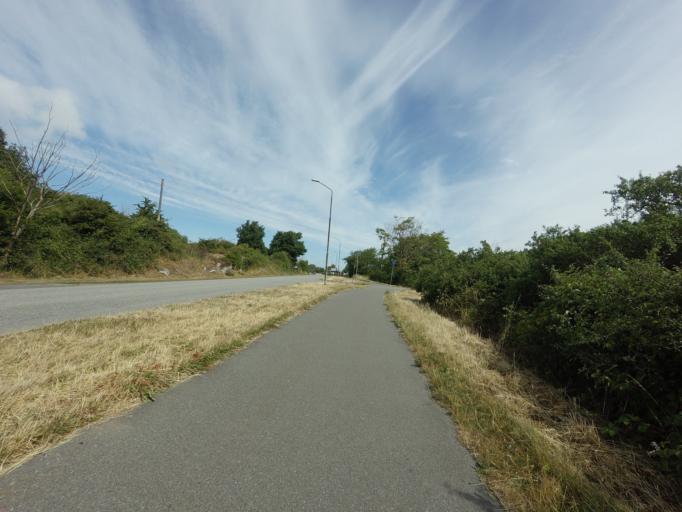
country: SE
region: Skane
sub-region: Simrishamns Kommun
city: Simrishamn
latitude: 55.5379
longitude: 14.3555
